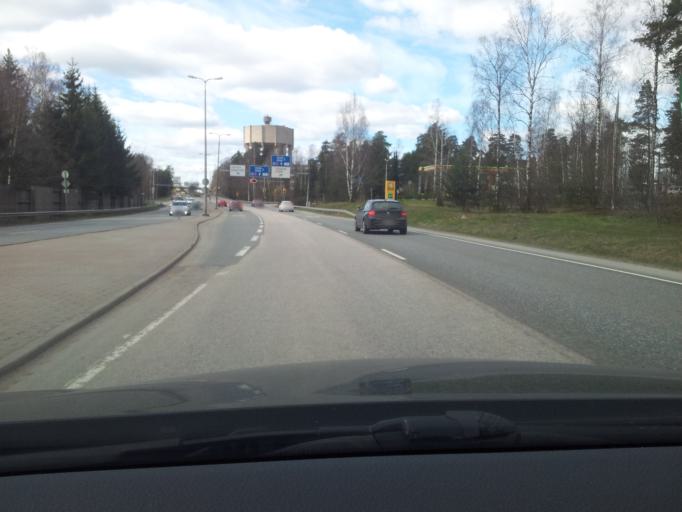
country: FI
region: Uusimaa
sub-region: Helsinki
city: Otaniemi
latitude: 60.1783
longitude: 24.8259
